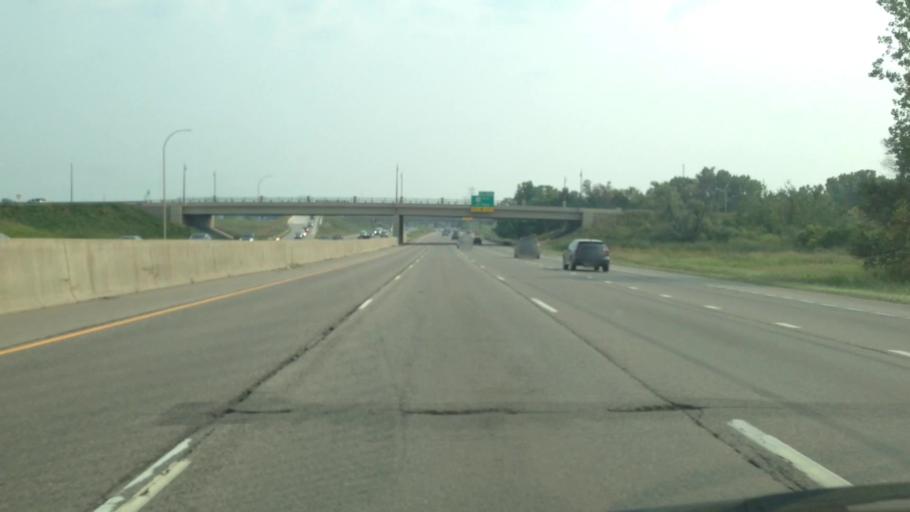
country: US
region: Minnesota
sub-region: Ramsey County
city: Mounds View
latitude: 45.0971
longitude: -93.1884
